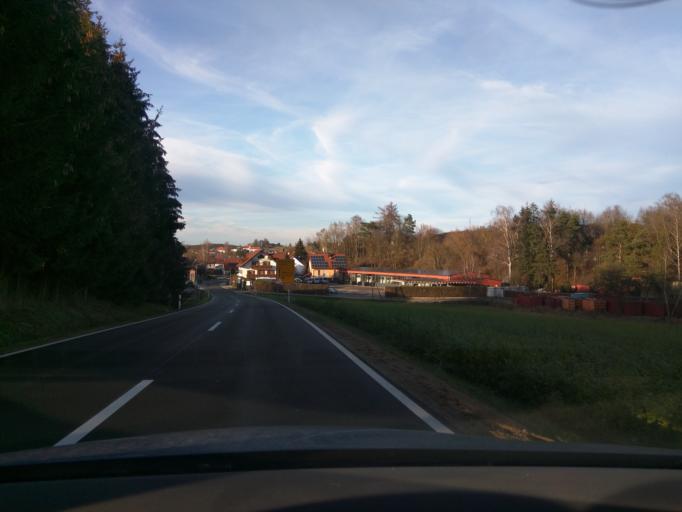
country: DE
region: Bavaria
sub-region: Upper Bavaria
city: Au in der Hallertau
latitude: 48.5512
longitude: 11.7486
